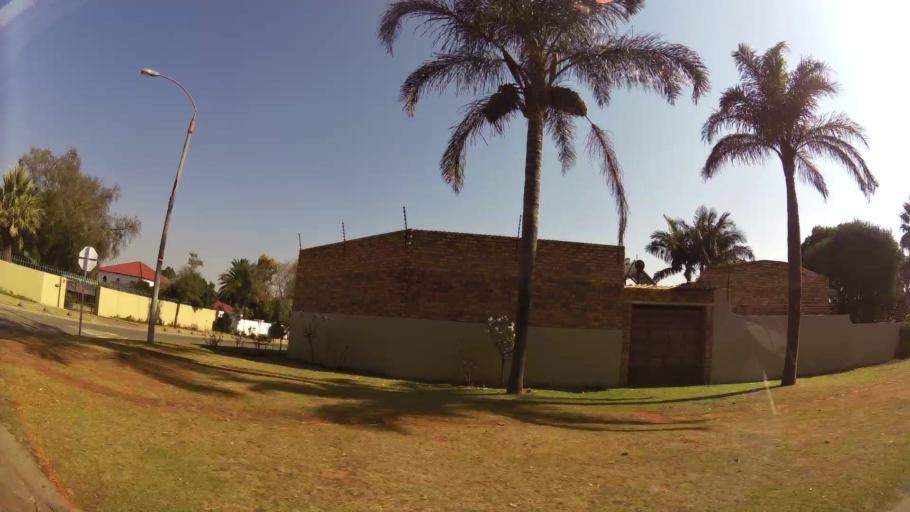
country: ZA
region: Gauteng
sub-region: Ekurhuleni Metropolitan Municipality
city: Boksburg
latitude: -26.2482
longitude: 28.2757
